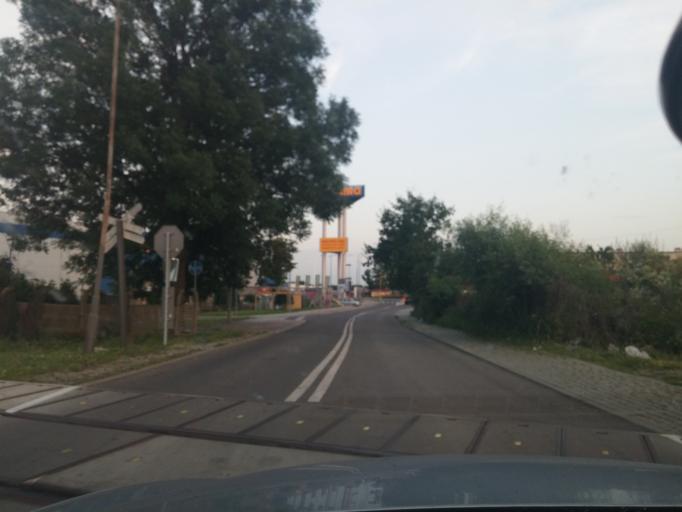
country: PL
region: Subcarpathian Voivodeship
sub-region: Przemysl
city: Przemysl
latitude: 49.7846
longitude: 22.8053
